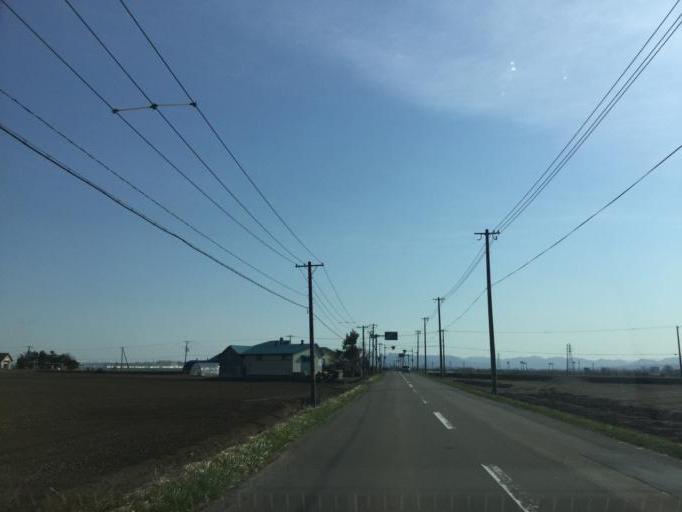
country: JP
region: Hokkaido
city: Iwamizawa
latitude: 43.1958
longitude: 141.7257
